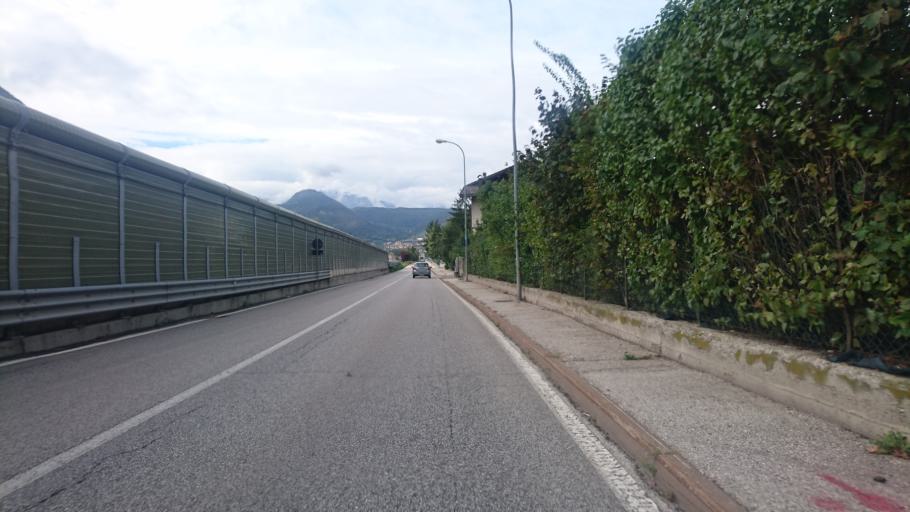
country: IT
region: Trentino-Alto Adige
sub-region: Provincia di Trento
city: Madrano-Canzolino
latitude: 46.0729
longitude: 11.2151
